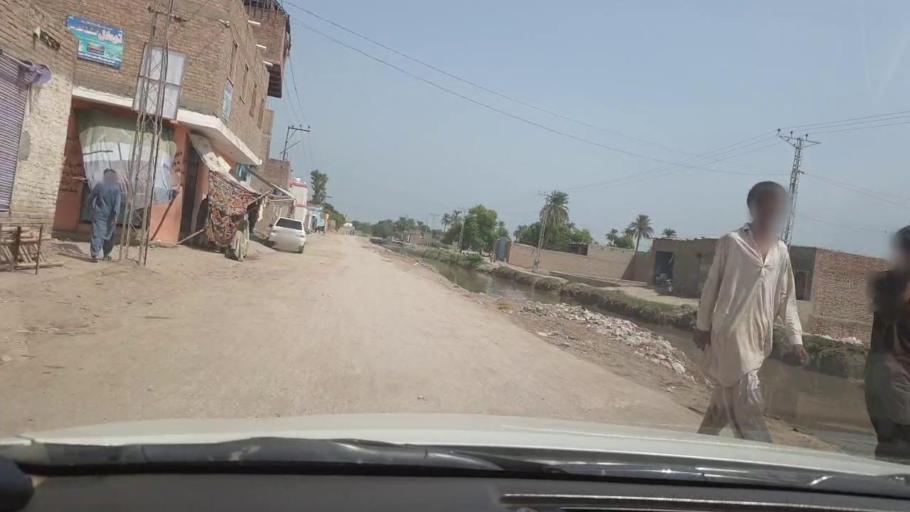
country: PK
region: Sindh
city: Shikarpur
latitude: 27.9442
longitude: 68.6345
